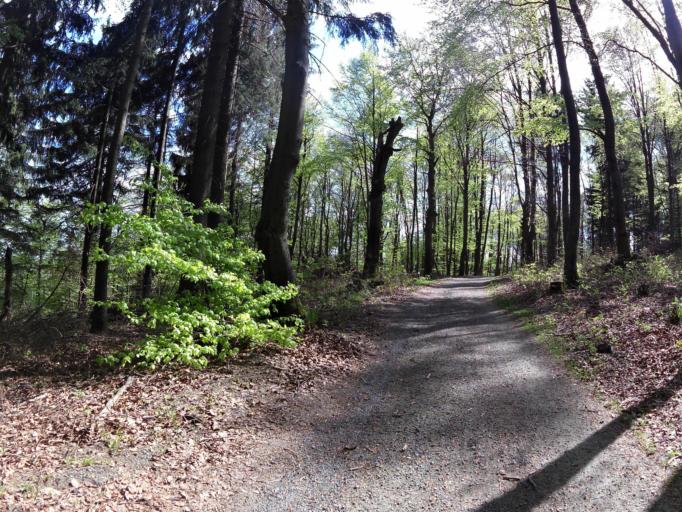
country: DE
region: Thuringia
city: Finsterbergen
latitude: 50.7928
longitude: 10.5414
